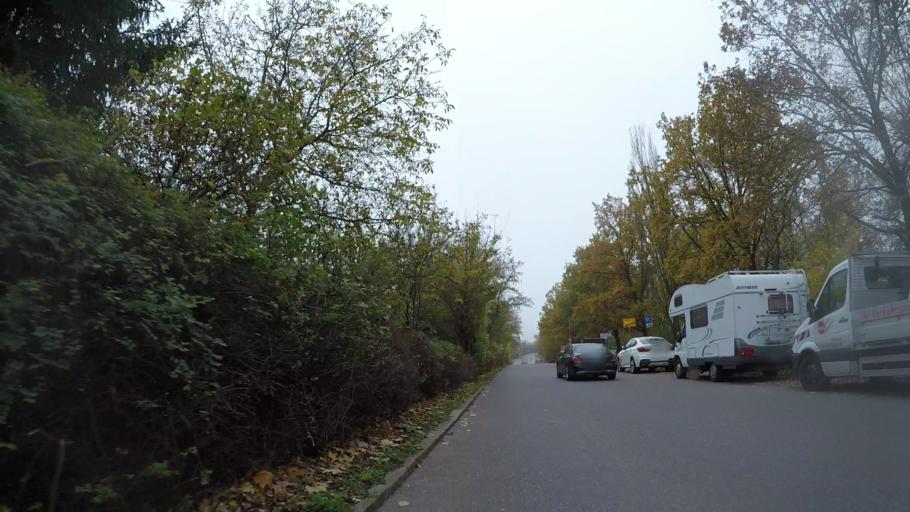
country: DE
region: Baden-Wuerttemberg
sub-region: Tuebingen Region
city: Reutlingen
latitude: 48.5226
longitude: 9.2176
